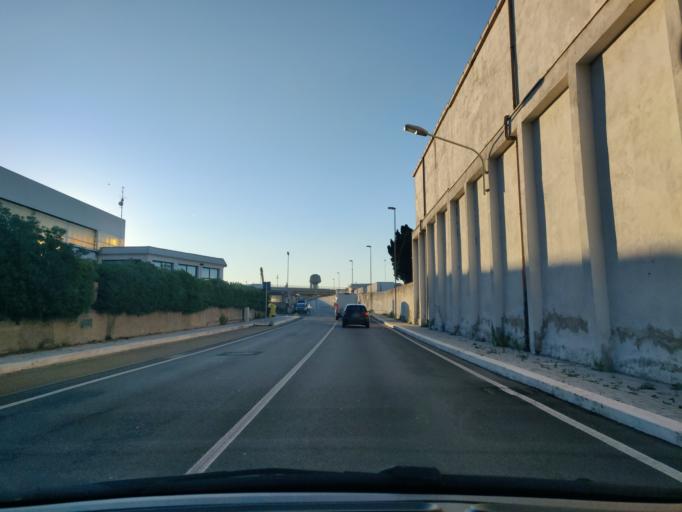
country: IT
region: Latium
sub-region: Citta metropolitana di Roma Capitale
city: Civitavecchia
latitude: 42.1058
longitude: 11.7833
